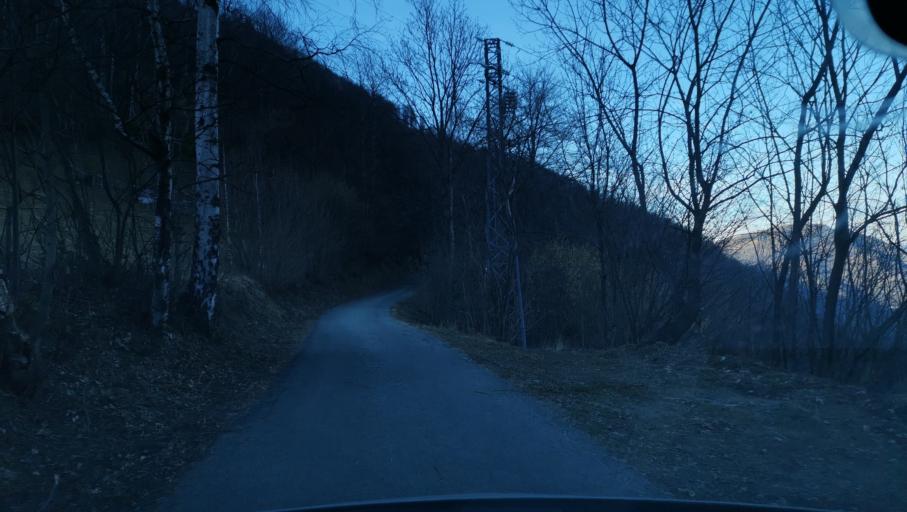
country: IT
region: Piedmont
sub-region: Provincia di Torino
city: Rora
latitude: 44.7735
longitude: 7.1987
